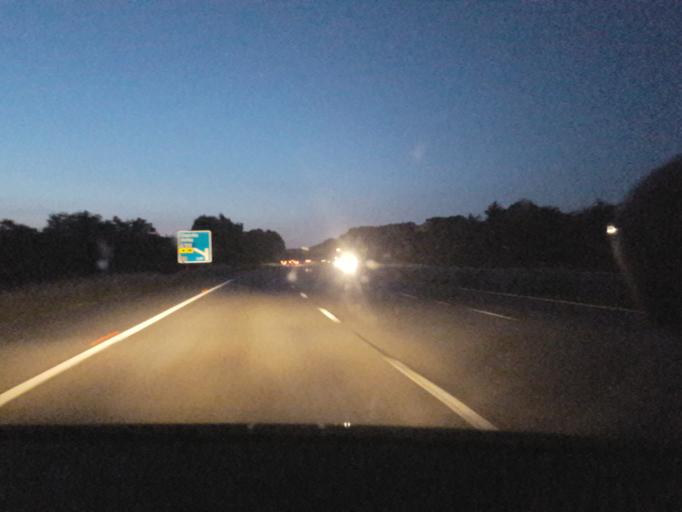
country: GB
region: England
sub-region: Leicestershire
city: Markfield
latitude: 52.6824
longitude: -1.2892
